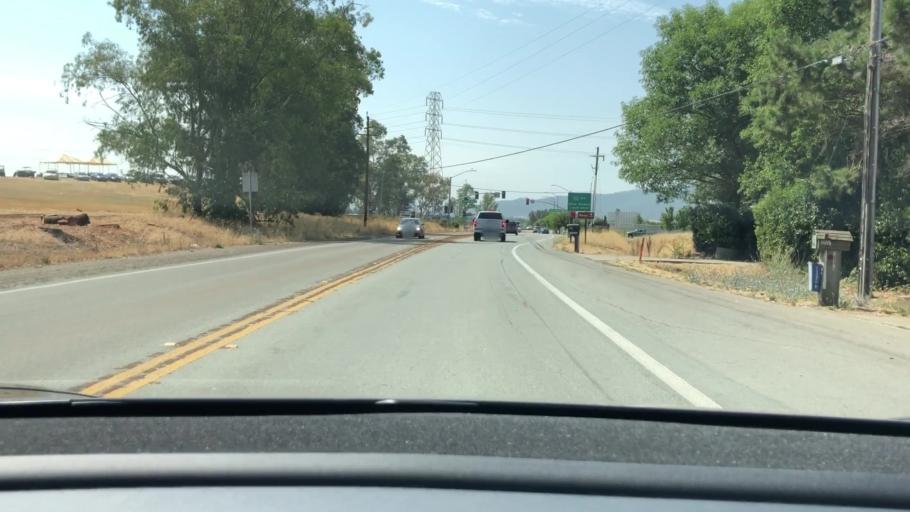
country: US
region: California
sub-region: Santa Clara County
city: Gilroy
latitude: 37.0392
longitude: -121.5980
